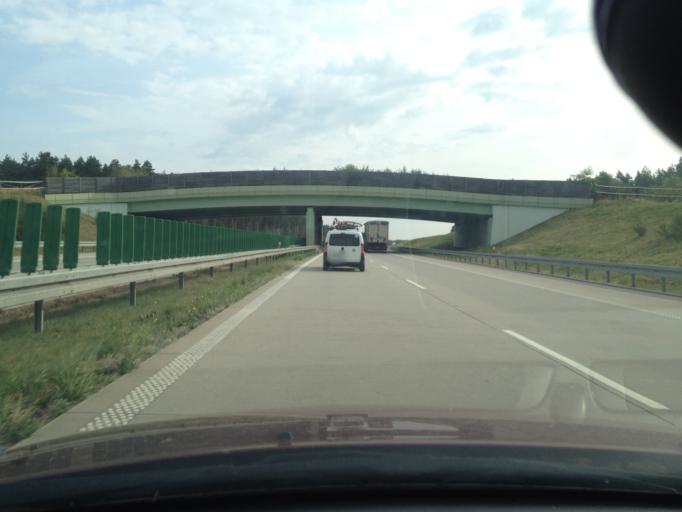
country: PL
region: Lower Silesian Voivodeship
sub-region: Powiat boleslawiecki
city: Nowogrodziec
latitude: 51.2640
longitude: 15.3679
